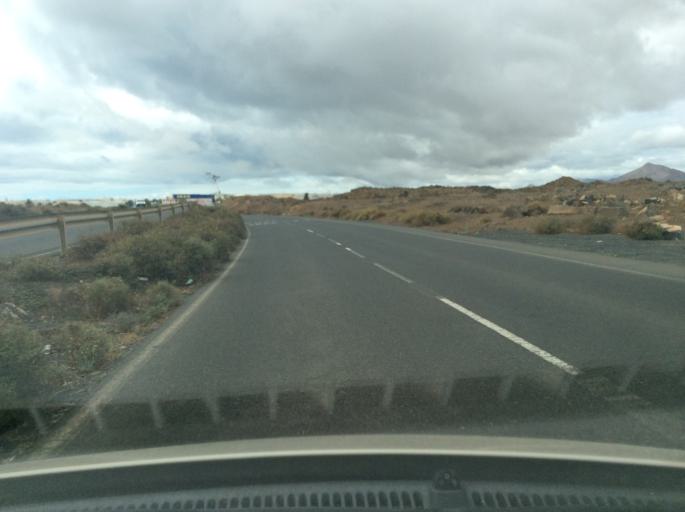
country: ES
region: Canary Islands
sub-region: Provincia de Las Palmas
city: Arrecife
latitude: 28.9800
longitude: -13.5280
